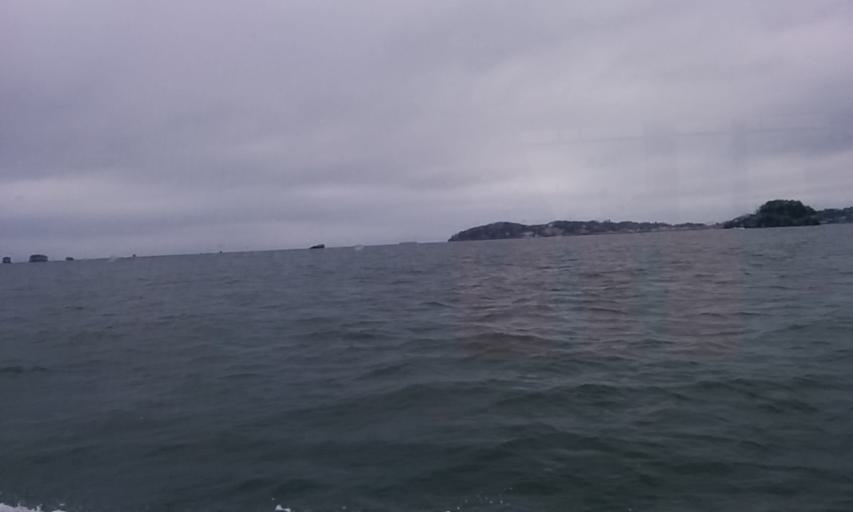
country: JP
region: Miyagi
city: Shiogama
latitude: 38.3237
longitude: 141.0905
